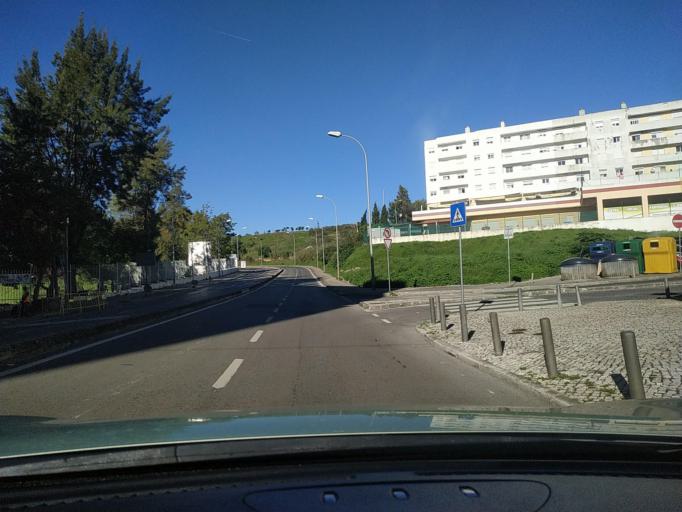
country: PT
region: Lisbon
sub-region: Amadora
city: Amadora
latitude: 38.7692
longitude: -9.2300
